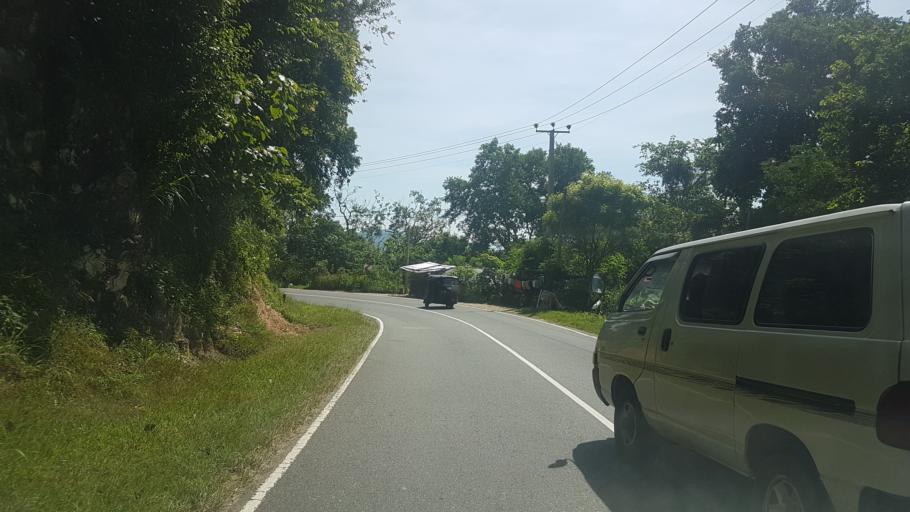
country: LK
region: Uva
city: Haputale
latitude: 6.8020
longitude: 81.0943
